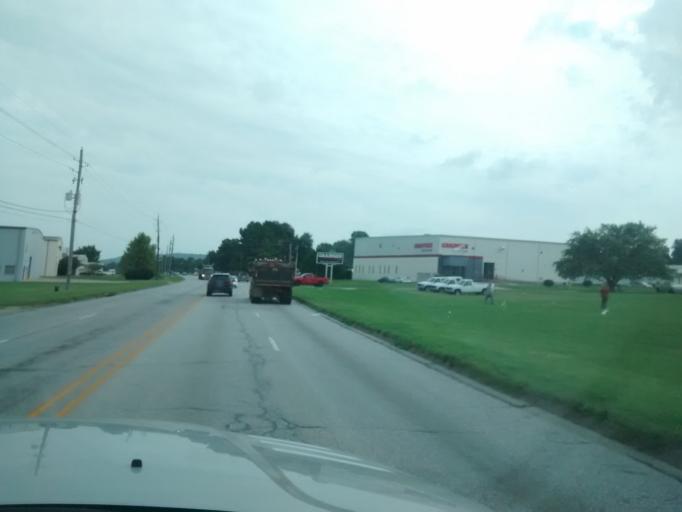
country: US
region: Arkansas
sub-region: Washington County
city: Springdale
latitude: 36.1724
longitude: -94.1178
